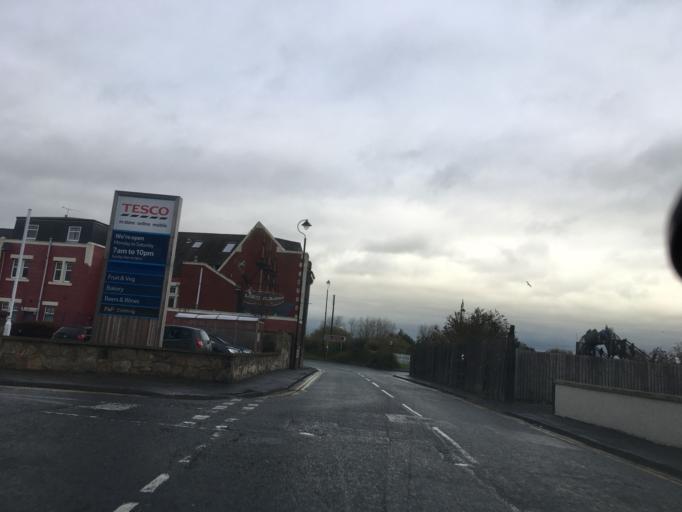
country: GB
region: Scotland
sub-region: Falkirk
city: Bo'ness
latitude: 56.0176
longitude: -3.6030
